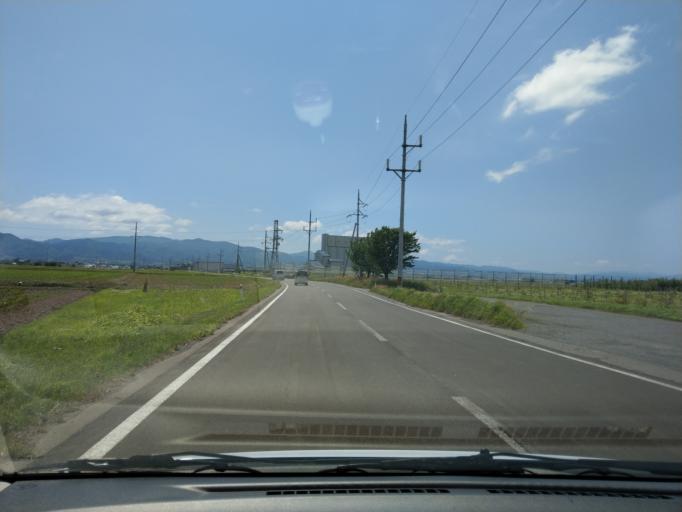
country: JP
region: Aomori
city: Kuroishi
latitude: 40.6024
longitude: 140.5568
